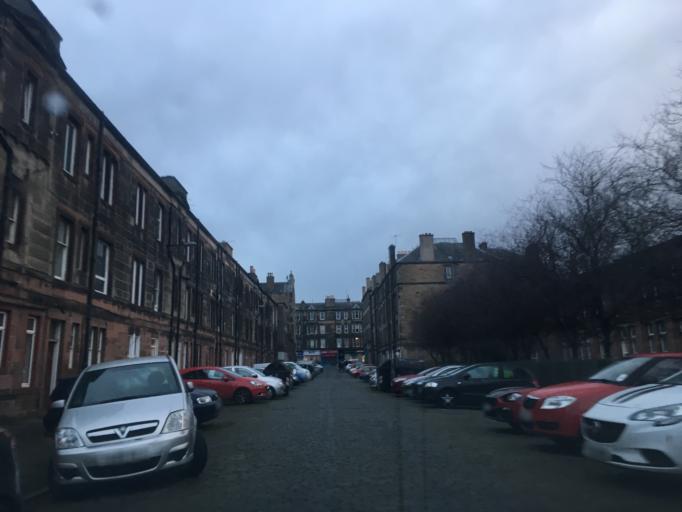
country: GB
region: Scotland
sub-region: West Lothian
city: Seafield
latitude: 55.9593
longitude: -3.1693
